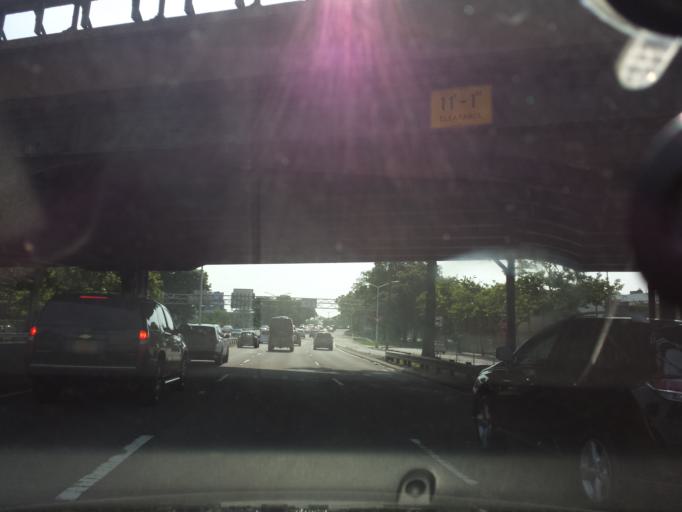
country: US
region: New York
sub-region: Kings County
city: Coney Island
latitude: 40.5850
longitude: -73.9549
